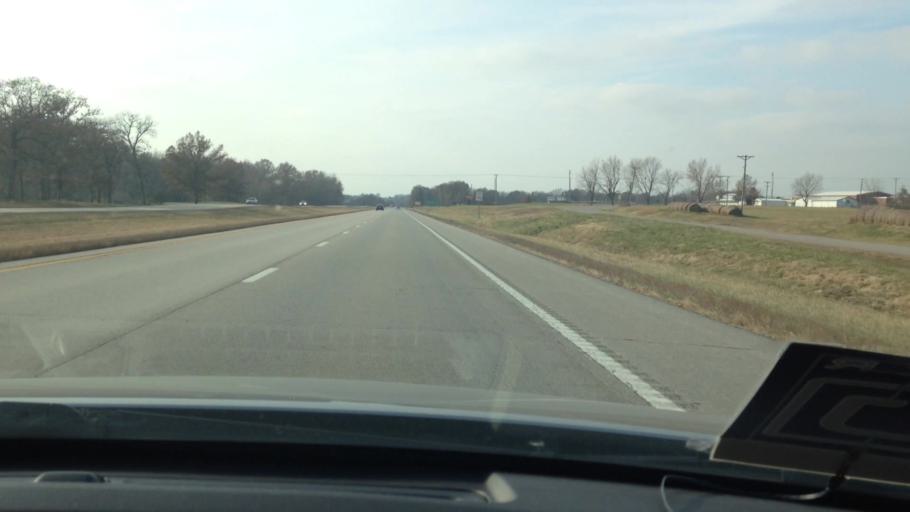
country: US
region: Missouri
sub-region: Cass County
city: Garden City
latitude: 38.5040
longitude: -94.0820
